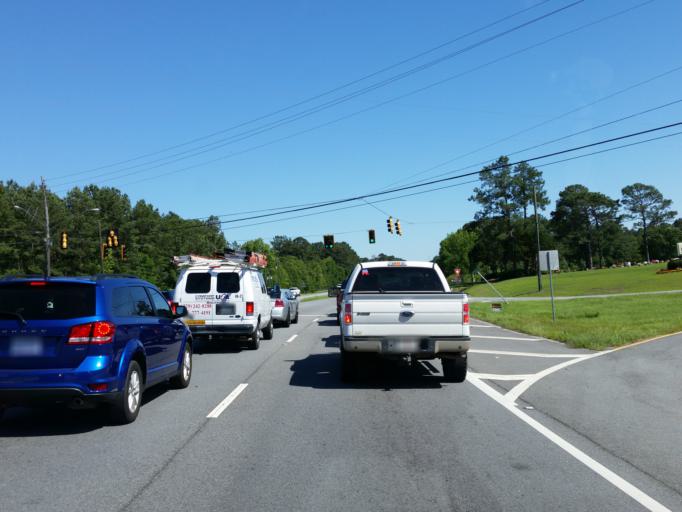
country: US
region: Georgia
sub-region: Lowndes County
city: Remerton
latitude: 30.8956
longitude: -83.3215
